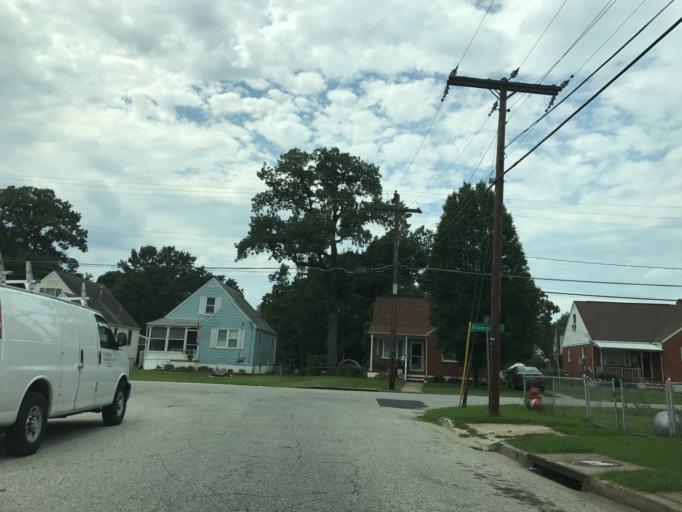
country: US
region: Maryland
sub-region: Baltimore County
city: Essex
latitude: 39.3155
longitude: -76.4839
